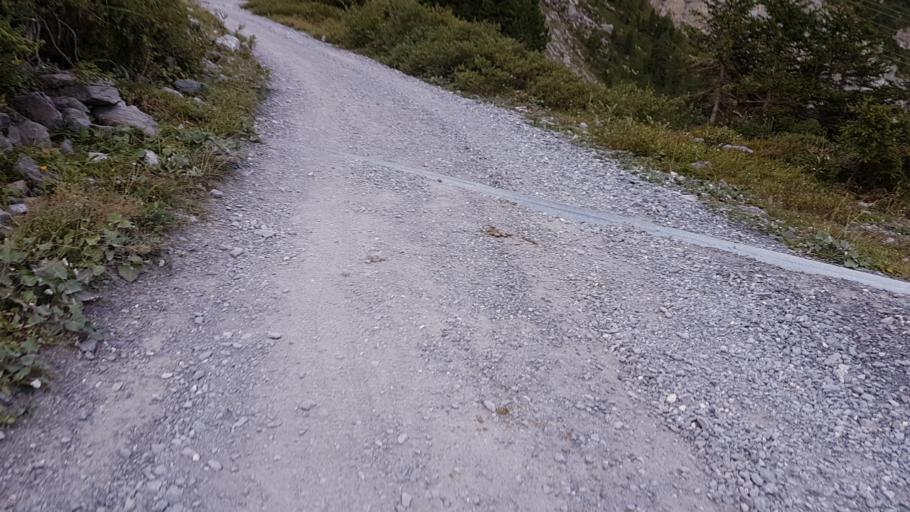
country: CH
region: Valais
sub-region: Leuk District
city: Leukerbad
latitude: 46.4358
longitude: 7.6343
